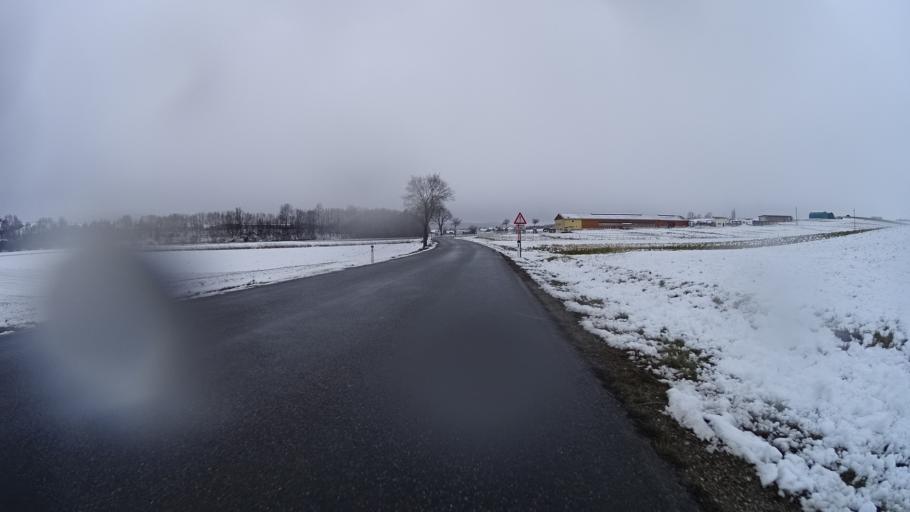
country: AT
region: Lower Austria
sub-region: Politischer Bezirk Korneuburg
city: Leobendorf
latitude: 48.3941
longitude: 16.2865
